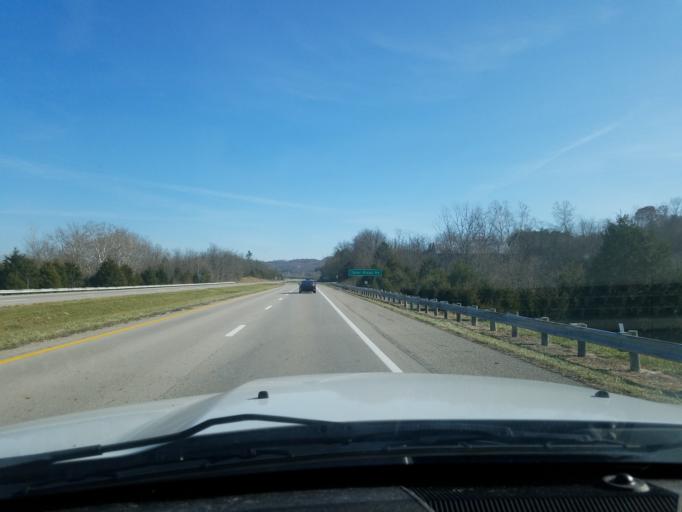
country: US
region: Ohio
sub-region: Adams County
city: Peebles
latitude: 38.9329
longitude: -83.4847
